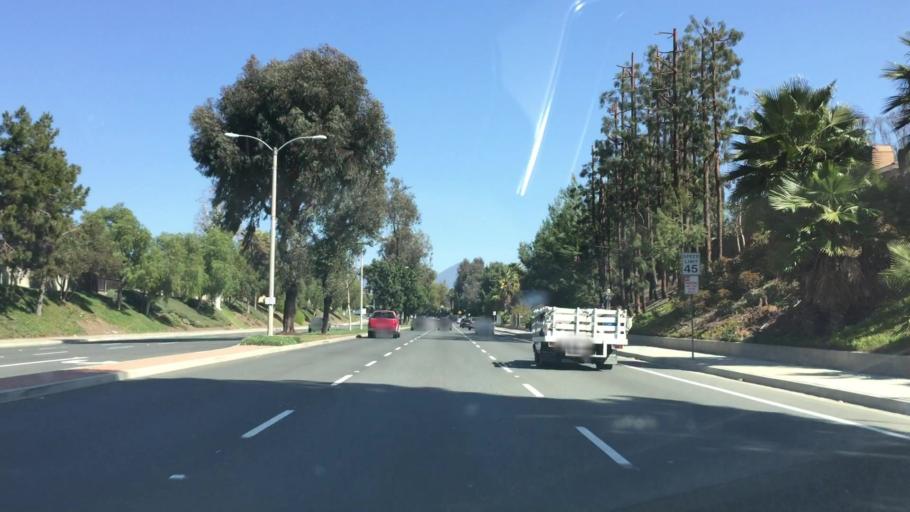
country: US
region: California
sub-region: Orange County
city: Mission Viejo
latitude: 33.5961
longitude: -117.6953
